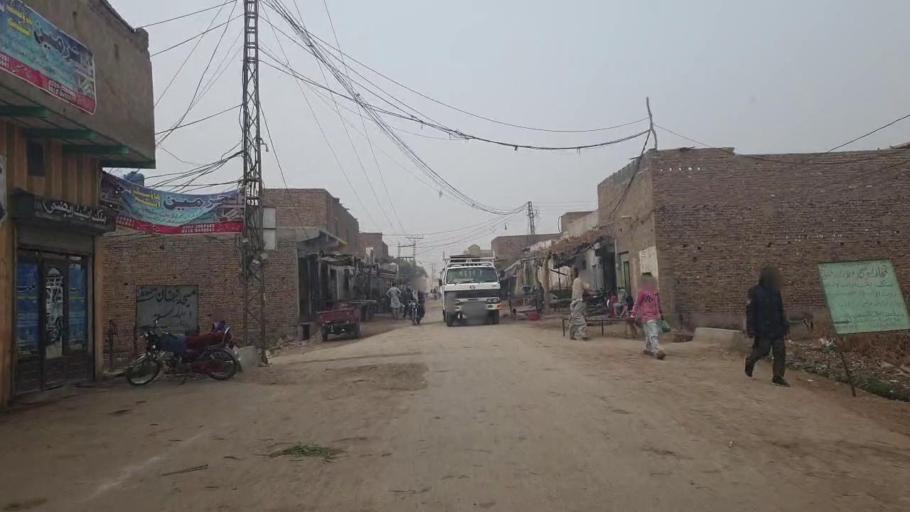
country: PK
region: Sindh
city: Tando Adam
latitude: 25.7532
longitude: 68.6674
